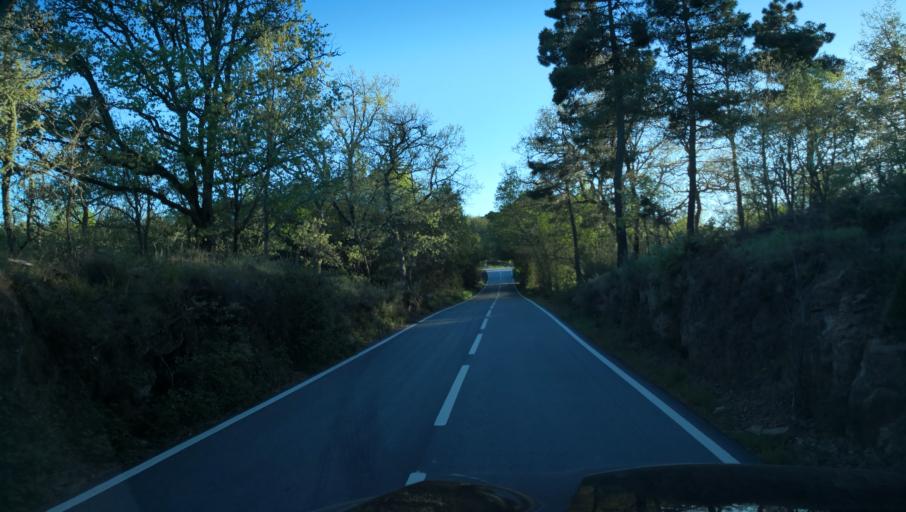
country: PT
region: Vila Real
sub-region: Sabrosa
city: Sabrosa
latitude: 41.3625
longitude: -7.6349
